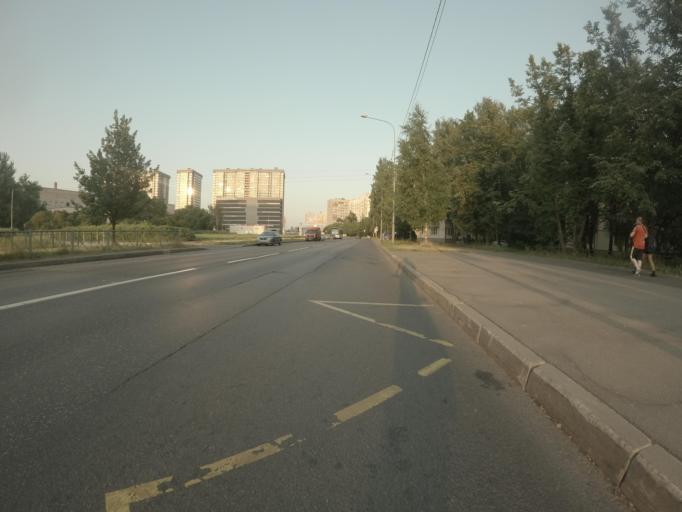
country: RU
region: Leningrad
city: Kalininskiy
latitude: 59.9777
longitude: 30.4304
